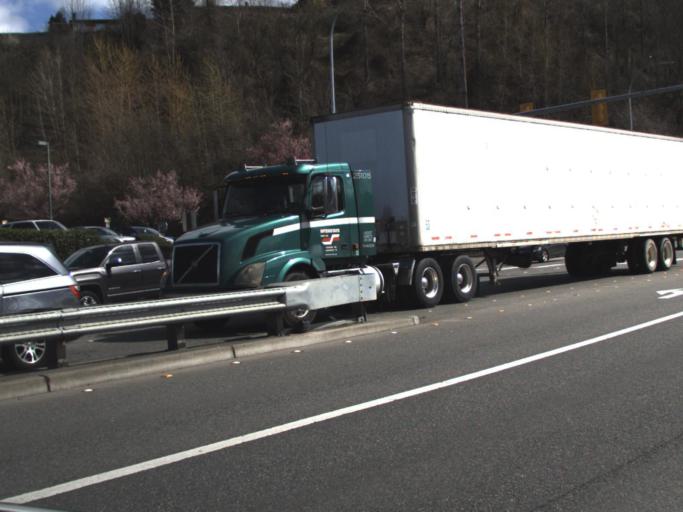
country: US
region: Washington
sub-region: King County
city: Renton
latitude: 47.4831
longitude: -122.1954
